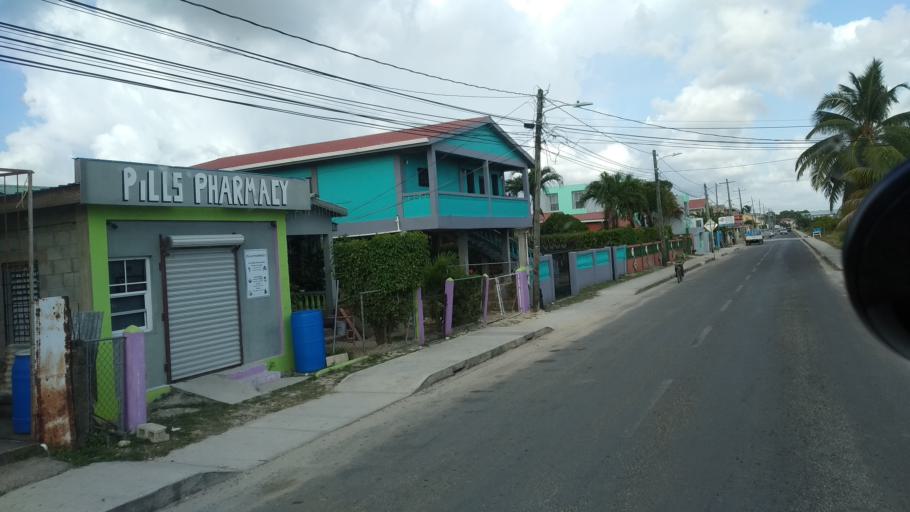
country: BZ
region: Belize
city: Belize City
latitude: 17.5113
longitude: -88.2237
